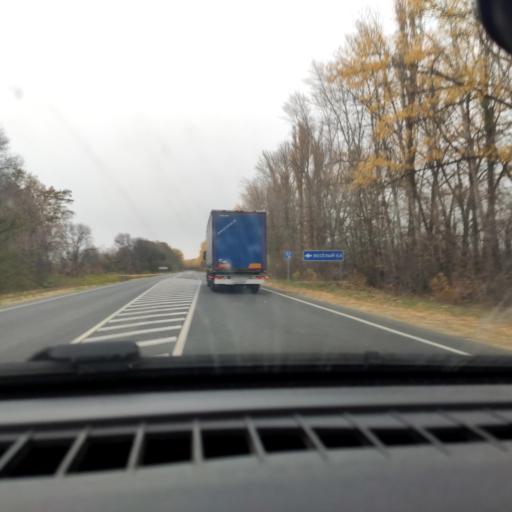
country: RU
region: Voronezj
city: Uryv-Pokrovka
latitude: 51.1798
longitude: 39.0811
